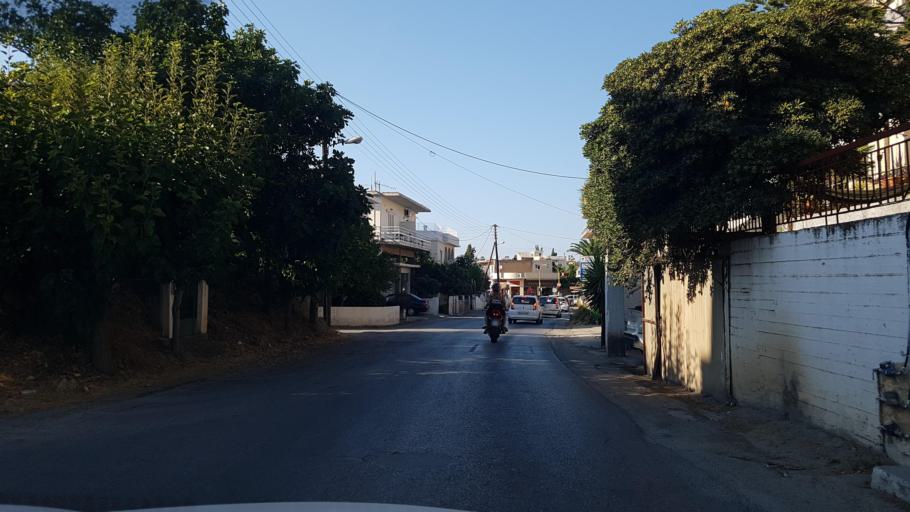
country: GR
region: Crete
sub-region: Nomos Chanias
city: Chania
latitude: 35.5030
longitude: 24.0194
